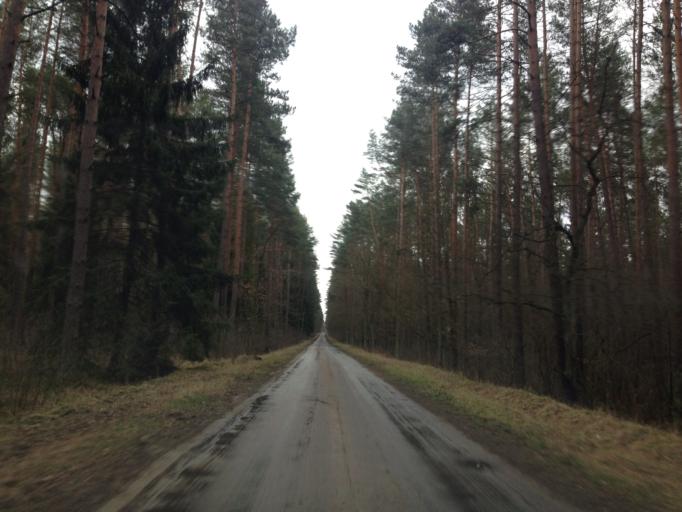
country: PL
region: Kujawsko-Pomorskie
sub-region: Powiat brodnicki
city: Gorzno
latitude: 53.1814
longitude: 19.7016
